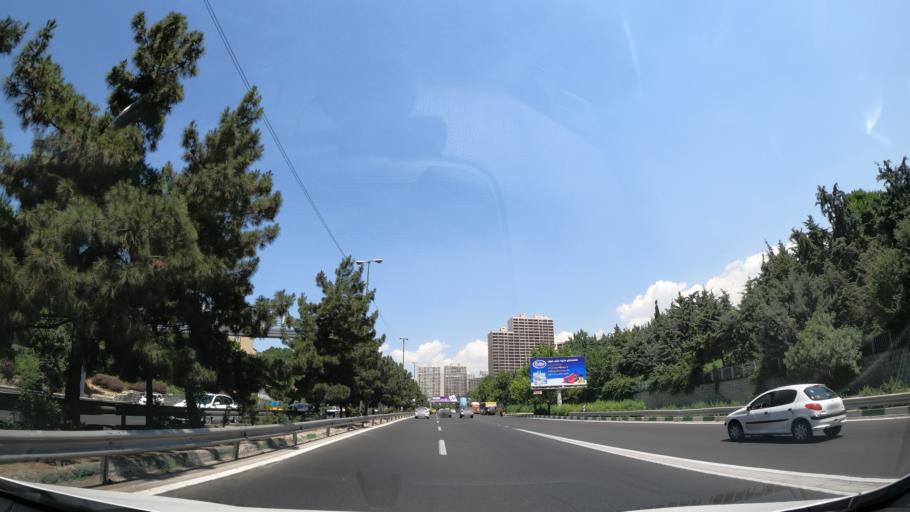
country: IR
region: Tehran
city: Tajrish
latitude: 35.7520
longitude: 51.3701
